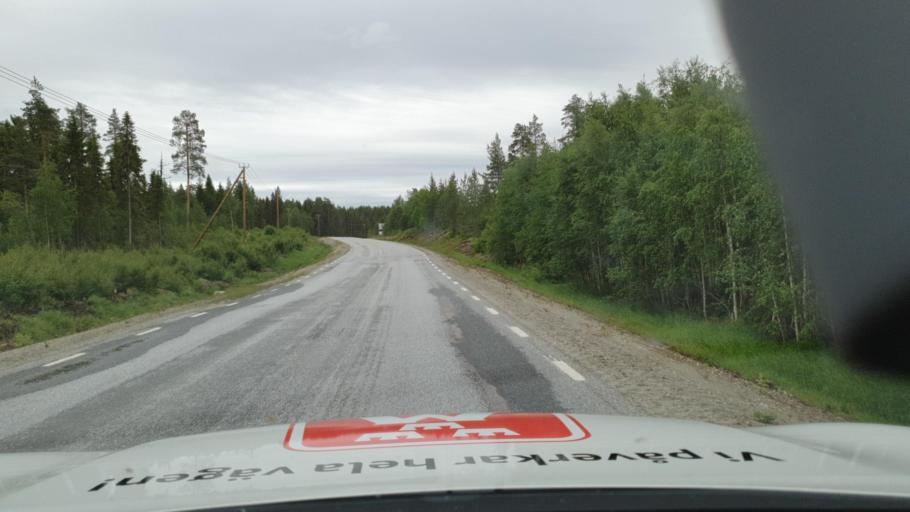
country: SE
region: Vaesterbotten
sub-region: Lycksele Kommun
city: Lycksele
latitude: 64.0882
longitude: 18.3913
